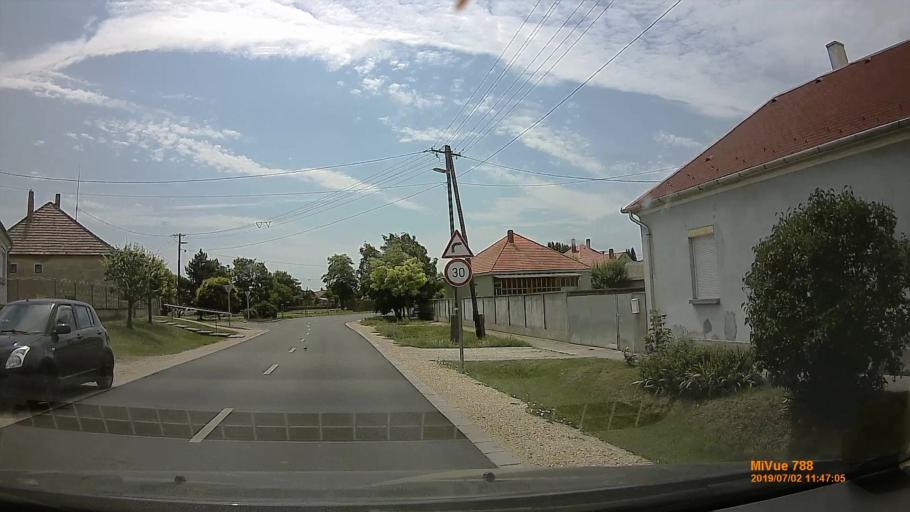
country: HU
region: Gyor-Moson-Sopron
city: Janossomorja
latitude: 47.8558
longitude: 17.1769
